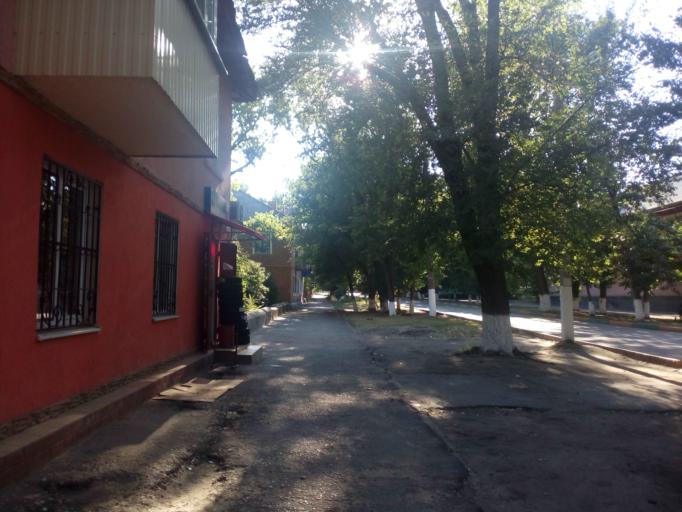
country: RU
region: Rostov
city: Sholokhovskiy
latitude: 48.2804
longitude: 41.0495
